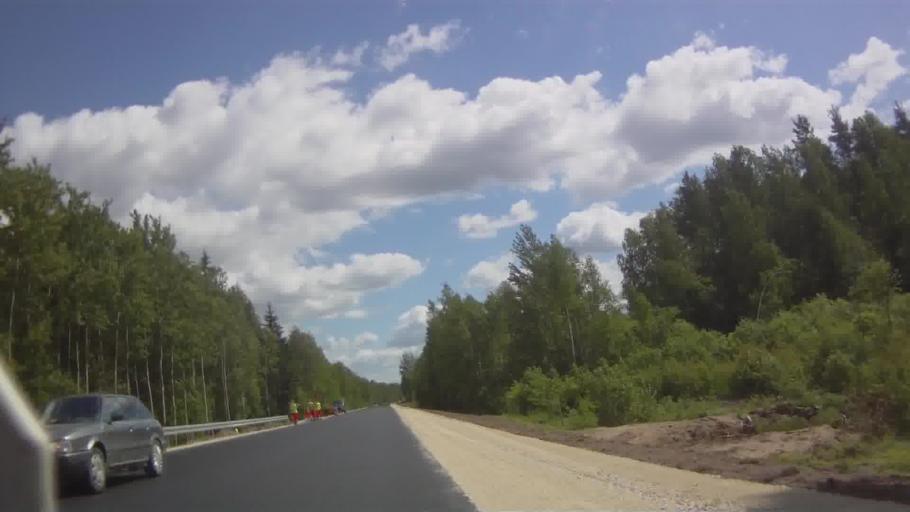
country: LV
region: Vilanu
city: Vilani
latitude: 56.5628
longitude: 27.0124
